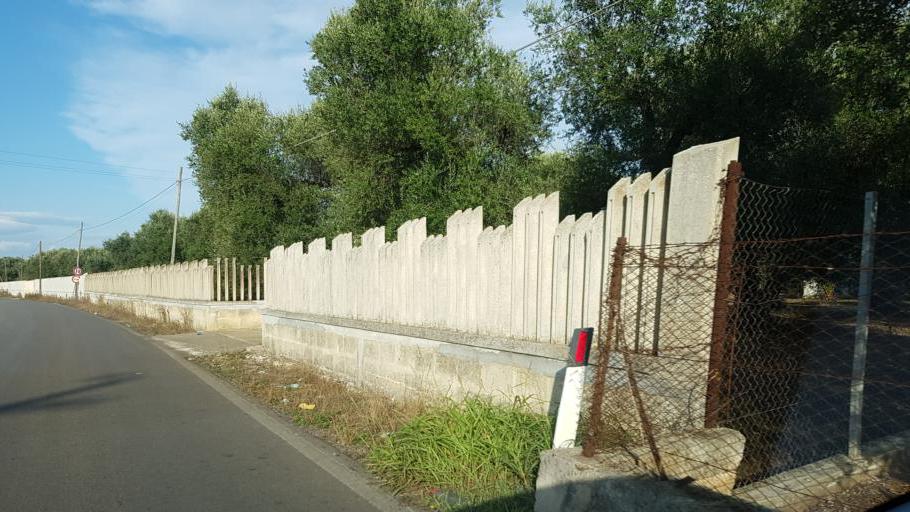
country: IT
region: Apulia
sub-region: Provincia di Brindisi
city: Oria
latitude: 40.5136
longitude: 17.6500
